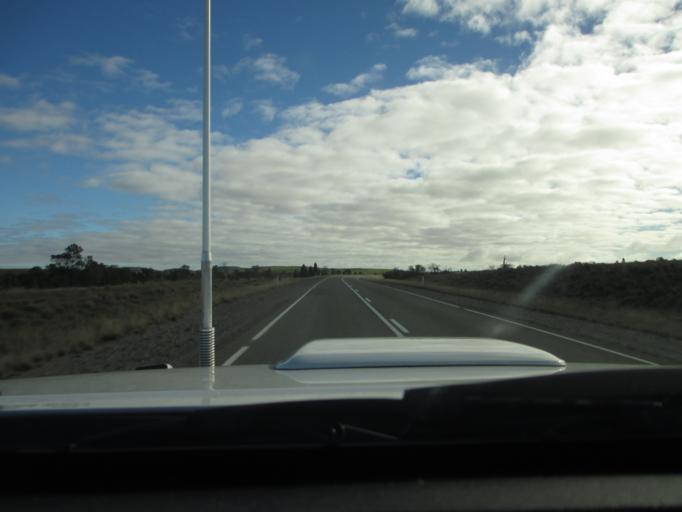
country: AU
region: South Australia
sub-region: Peterborough
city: Peterborough
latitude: -32.5894
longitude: 138.5605
